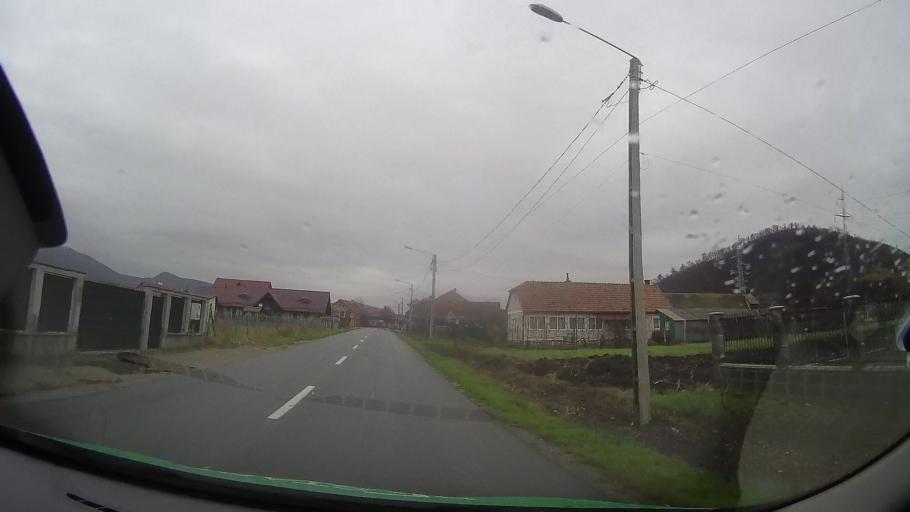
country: RO
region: Bistrita-Nasaud
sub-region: Municipiul Bistrita
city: Viisoara
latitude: 47.0674
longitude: 24.4376
